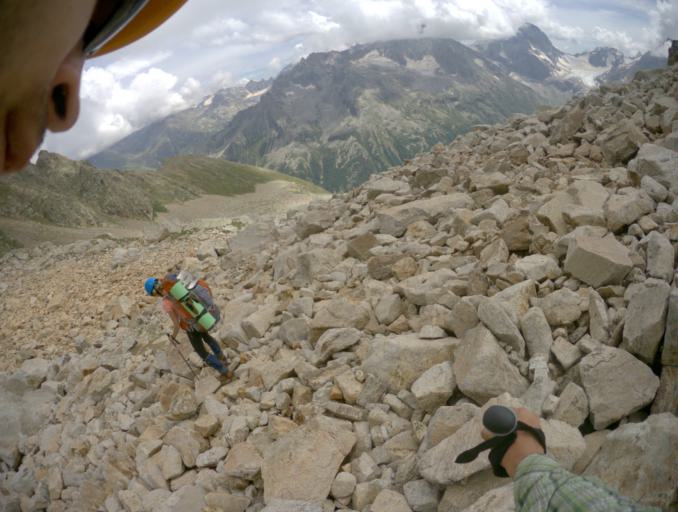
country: RU
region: Karachayevo-Cherkesiya
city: Uchkulan
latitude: 43.2759
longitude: 42.1201
